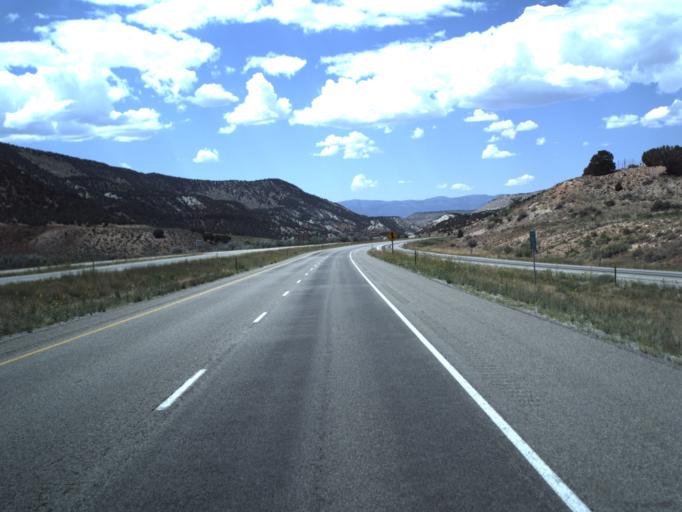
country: US
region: Utah
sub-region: Sevier County
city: Salina
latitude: 38.9170
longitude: -111.7430
